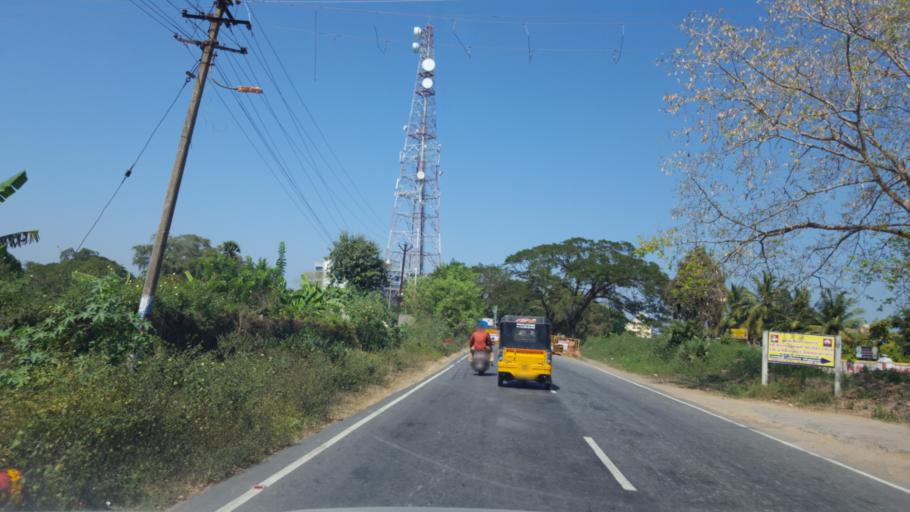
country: IN
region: Tamil Nadu
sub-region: Kancheepuram
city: Chengalpattu
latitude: 12.7342
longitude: 79.9438
